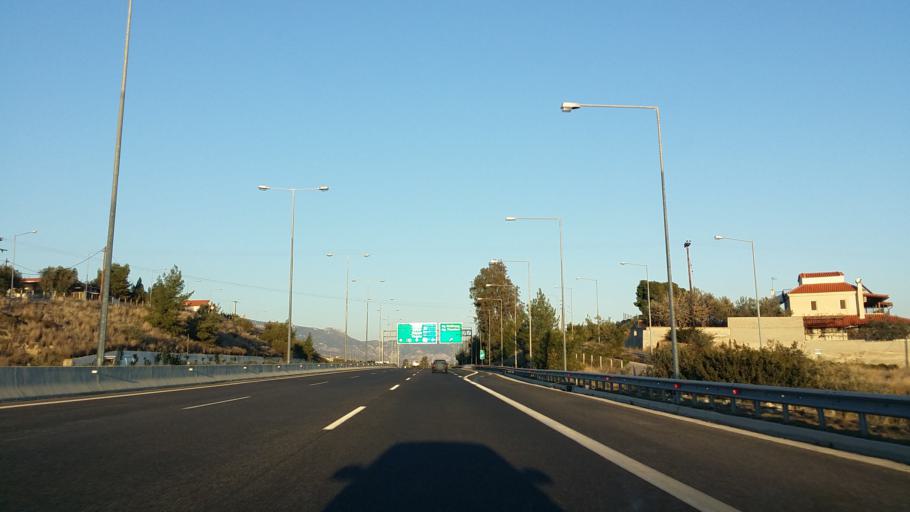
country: GR
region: Peloponnese
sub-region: Nomos Korinthias
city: Agioi Theodoroi
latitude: 37.9196
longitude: 23.1140
